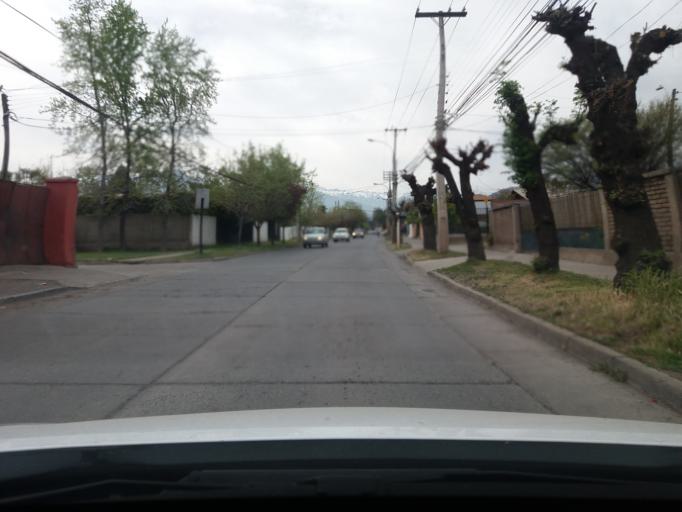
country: CL
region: Valparaiso
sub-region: Provincia de Los Andes
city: Los Andes
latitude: -32.8314
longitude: -70.6127
